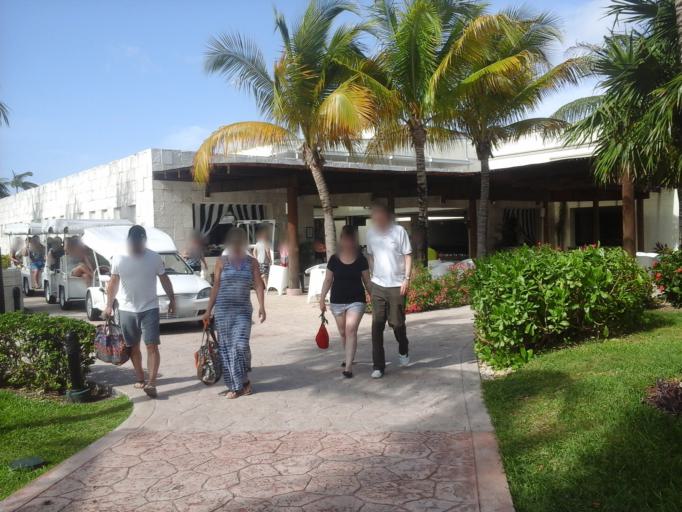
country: MX
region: Quintana Roo
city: Playa del Carmen
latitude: 20.7027
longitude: -87.0153
